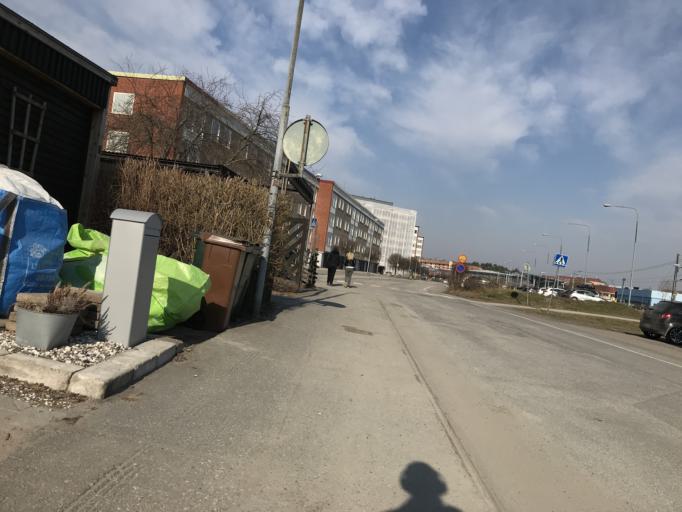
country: SE
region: Stockholm
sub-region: Osterakers Kommun
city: Akersberga
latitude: 59.4760
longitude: 18.3050
